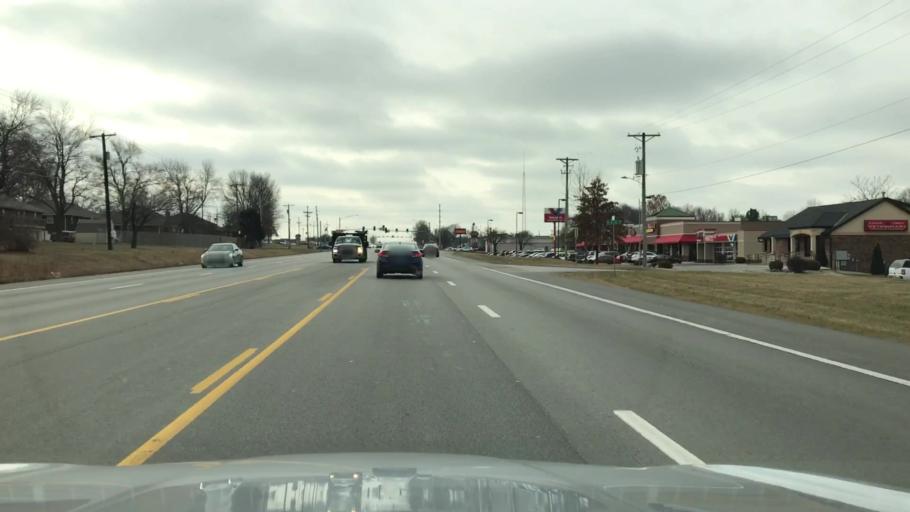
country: US
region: Missouri
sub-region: Jackson County
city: Lees Summit
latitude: 38.9125
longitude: -94.3625
